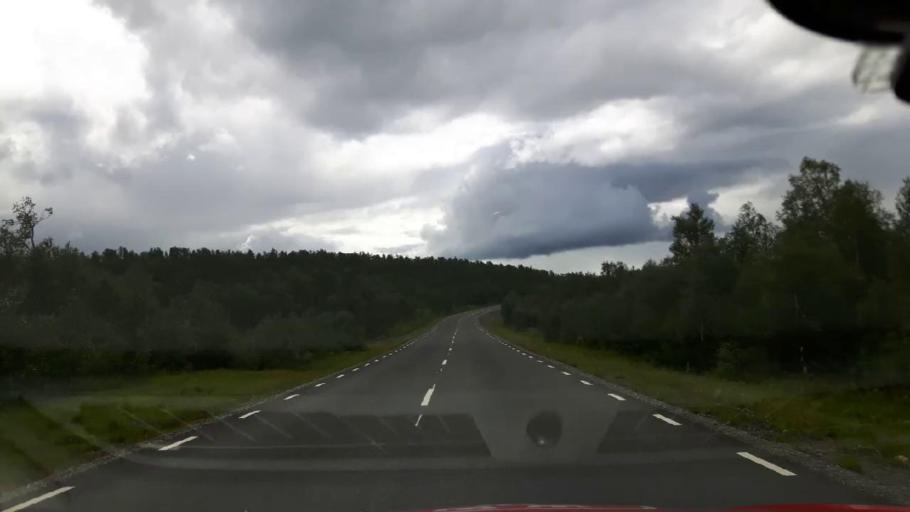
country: NO
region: Nord-Trondelag
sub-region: Royrvik
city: Royrvik
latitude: 64.9763
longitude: 14.2129
